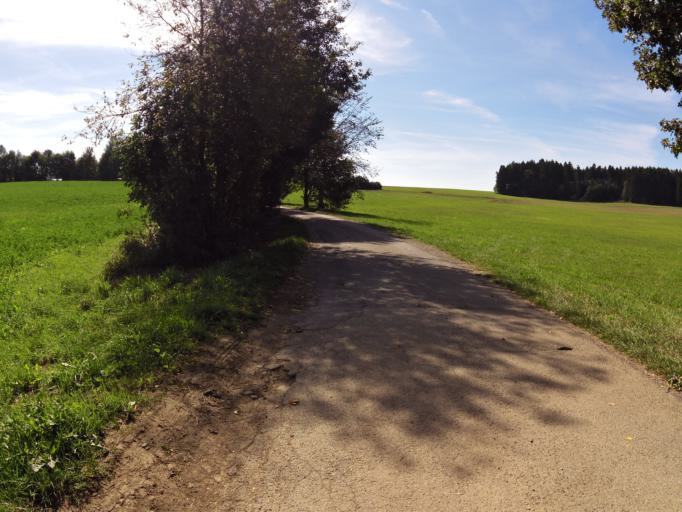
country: DE
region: Baden-Wuerttemberg
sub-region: Freiburg Region
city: Bad Durrheim
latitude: 48.0303
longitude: 8.5024
